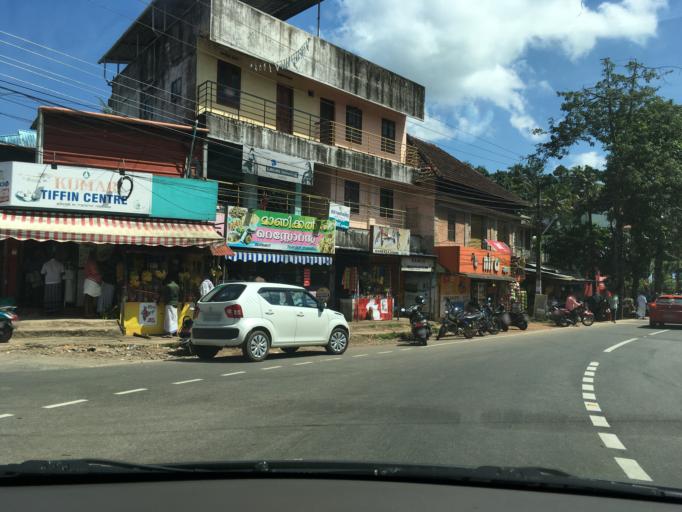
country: IN
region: Kerala
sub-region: Thiruvananthapuram
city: Nedumangad
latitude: 8.5752
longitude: 76.9966
